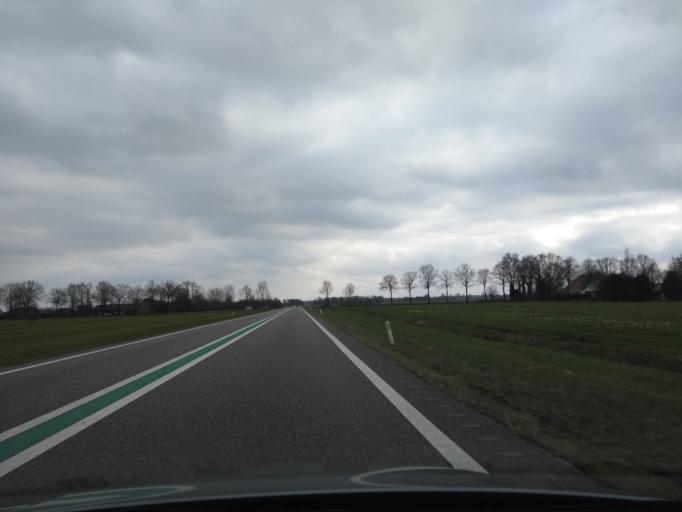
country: NL
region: Overijssel
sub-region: Gemeente Twenterand
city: Den Ham
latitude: 52.5777
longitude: 6.4159
